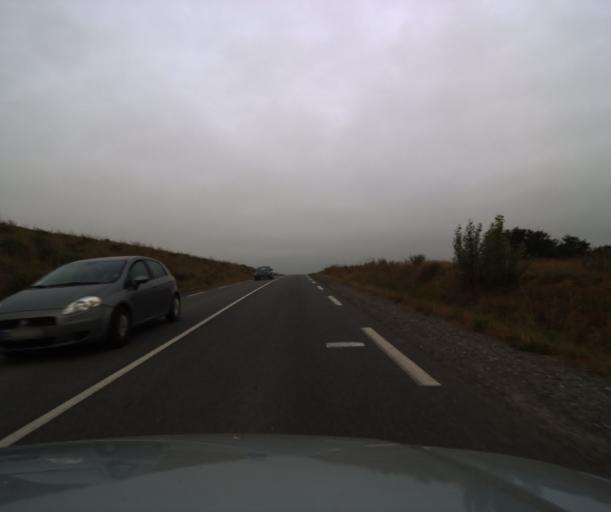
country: FR
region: Midi-Pyrenees
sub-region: Departement du Gers
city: Aubiet
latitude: 43.6482
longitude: 0.6987
